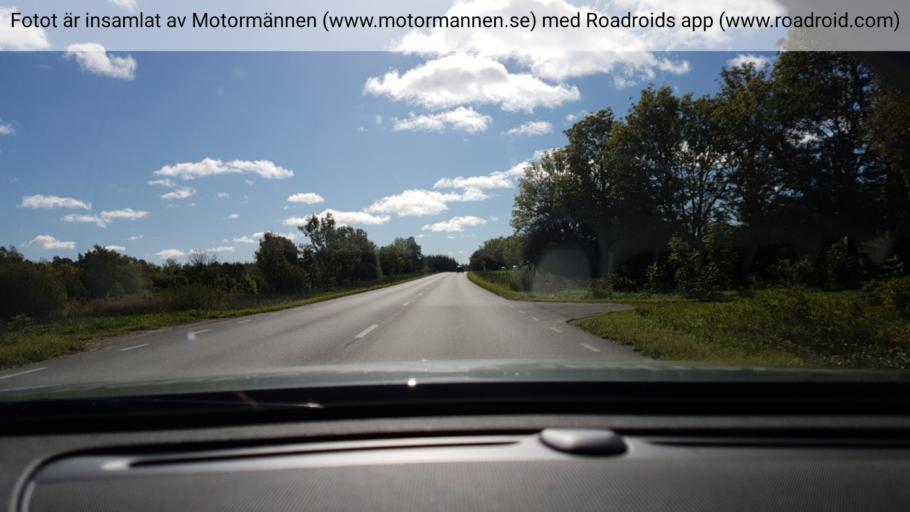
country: SE
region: Gotland
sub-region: Gotland
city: Slite
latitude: 57.7605
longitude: 18.7901
